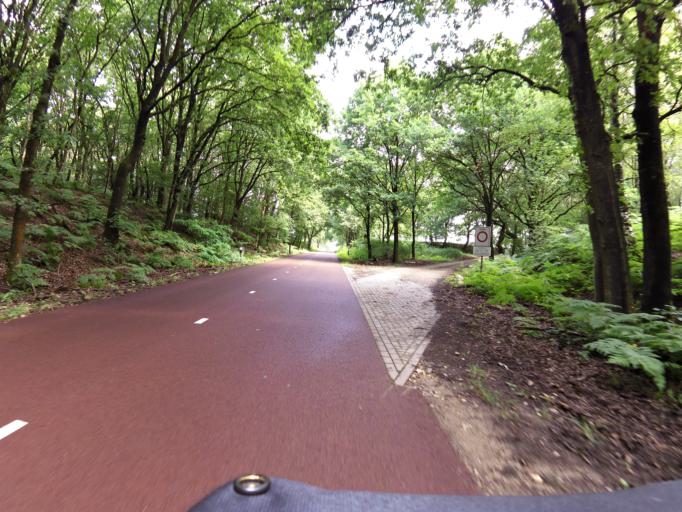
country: DE
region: North Rhine-Westphalia
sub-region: Regierungsbezirk Dusseldorf
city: Bruggen
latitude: 51.1781
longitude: 6.1438
